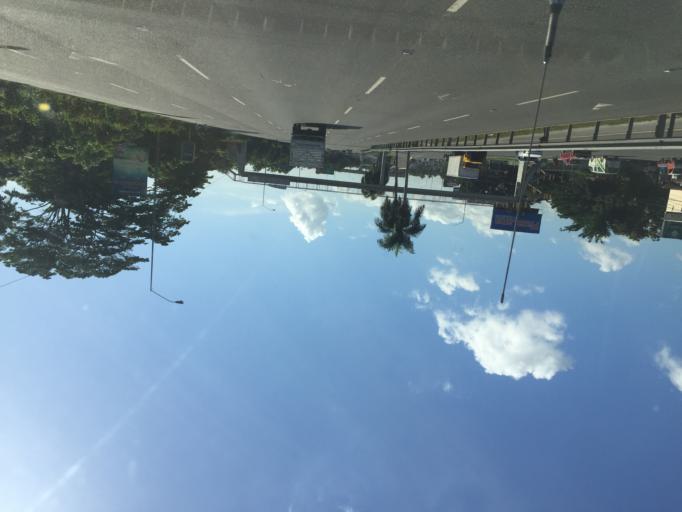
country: DO
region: Santo Domingo
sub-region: Santo Domingo
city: Boca Chica
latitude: 18.4509
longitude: -69.6863
